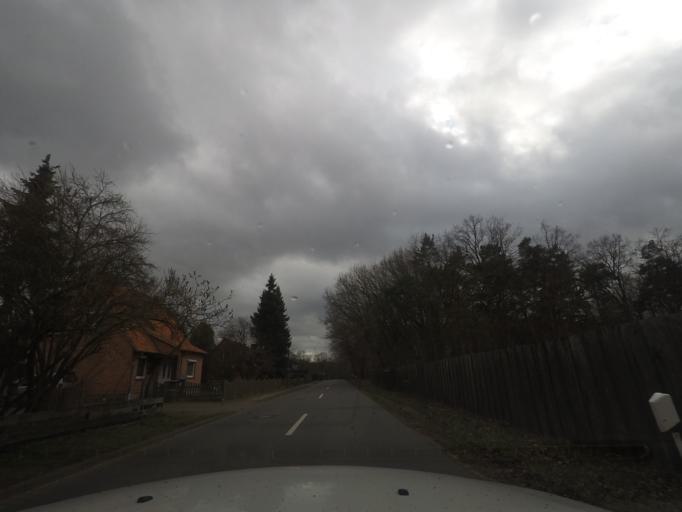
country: DE
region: Lower Saxony
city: Bad Bevensen
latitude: 53.0546
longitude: 10.6088
